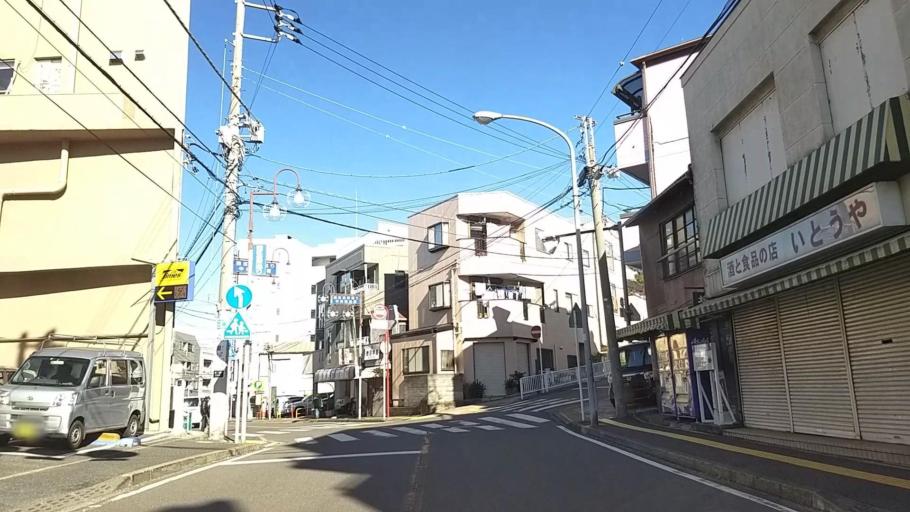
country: JP
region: Kanagawa
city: Yokohama
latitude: 35.4528
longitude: 139.6170
